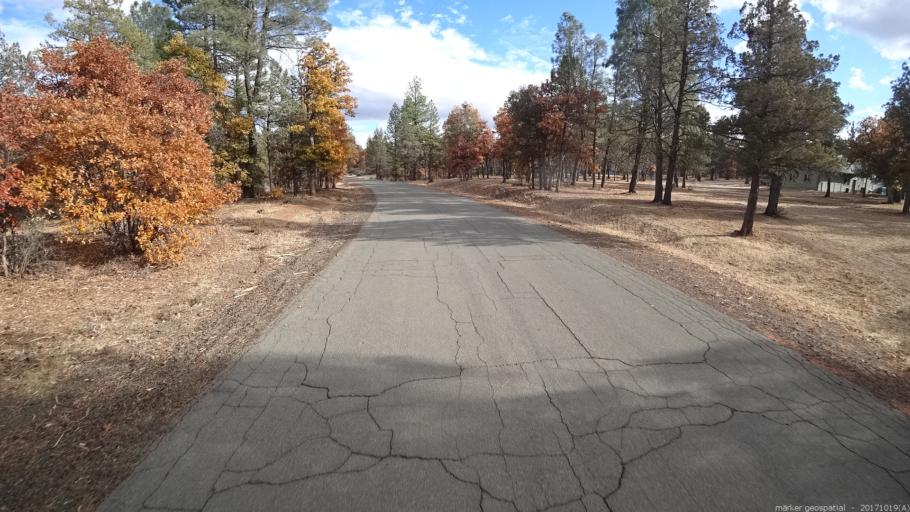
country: US
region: California
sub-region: Shasta County
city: Burney
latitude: 40.9722
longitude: -121.4436
